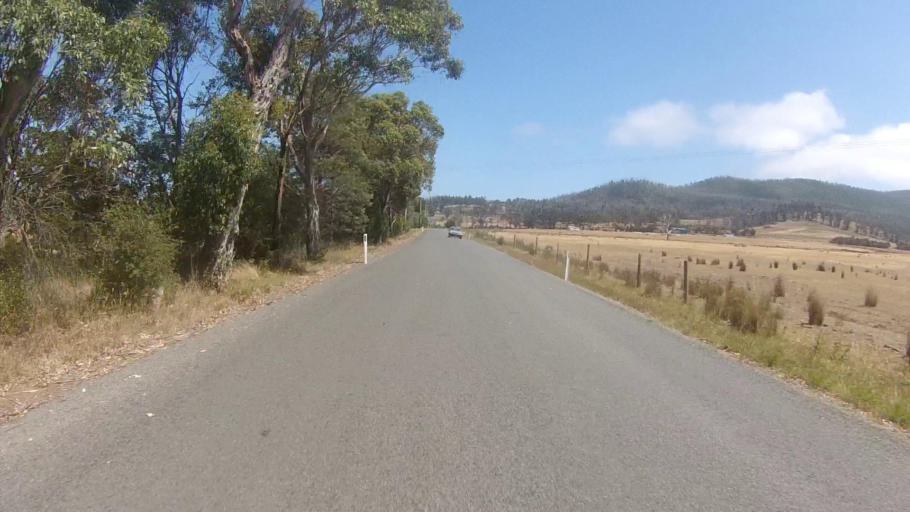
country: AU
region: Tasmania
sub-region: Sorell
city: Sorell
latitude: -42.8638
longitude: 147.8337
